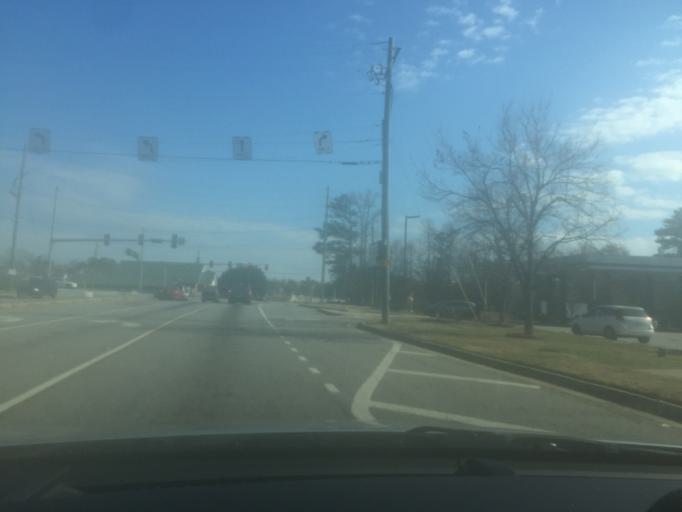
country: US
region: Georgia
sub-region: Clayton County
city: Riverdale
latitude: 33.5940
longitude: -84.4089
